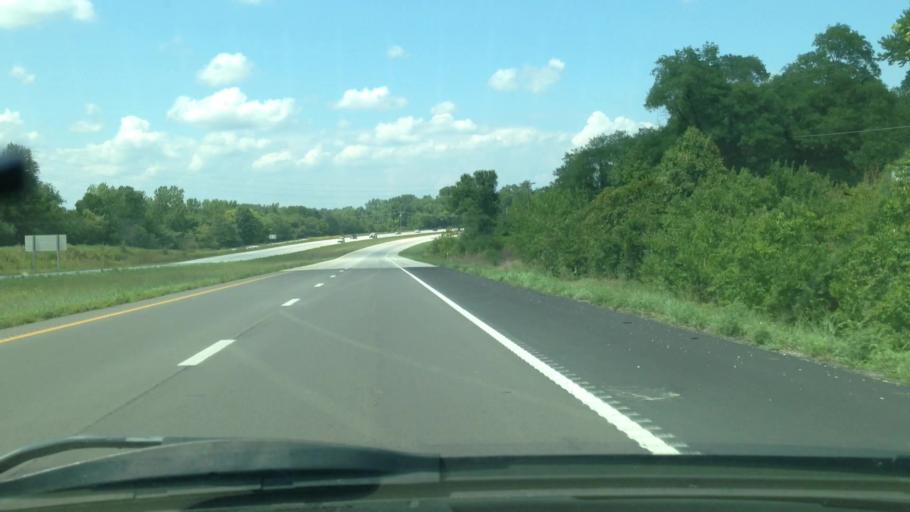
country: US
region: Missouri
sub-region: Lincoln County
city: Troy
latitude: 39.0026
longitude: -90.9746
